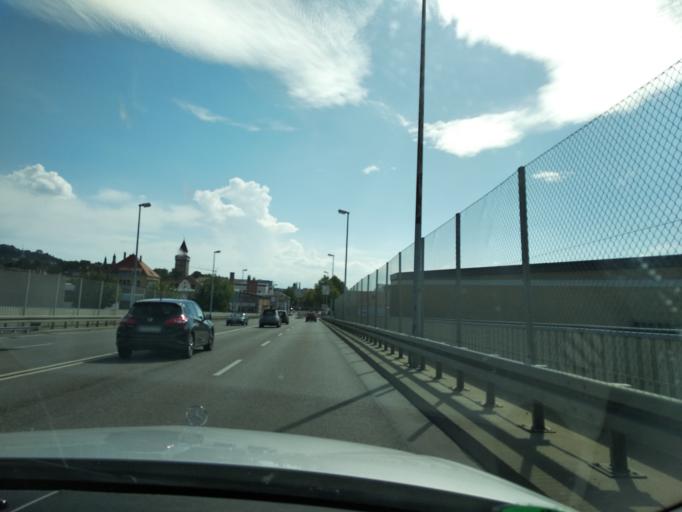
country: DE
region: Baden-Wuerttemberg
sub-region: Tuebingen Region
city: Ravensburg
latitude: 47.7892
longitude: 9.6114
